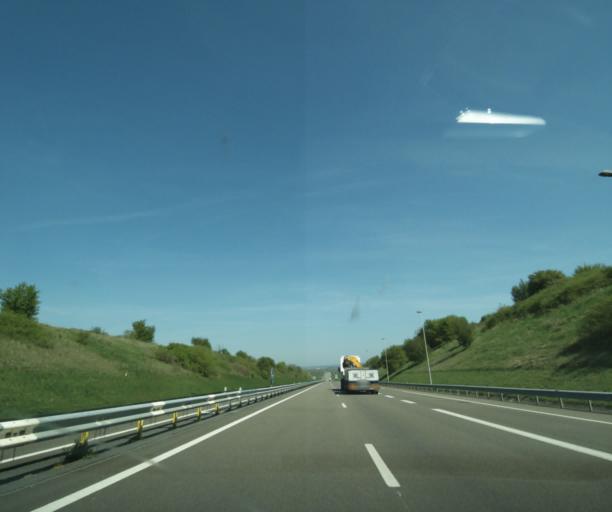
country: FR
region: Bourgogne
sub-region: Departement de la Nievre
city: Challuy
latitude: 46.9421
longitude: 3.1610
